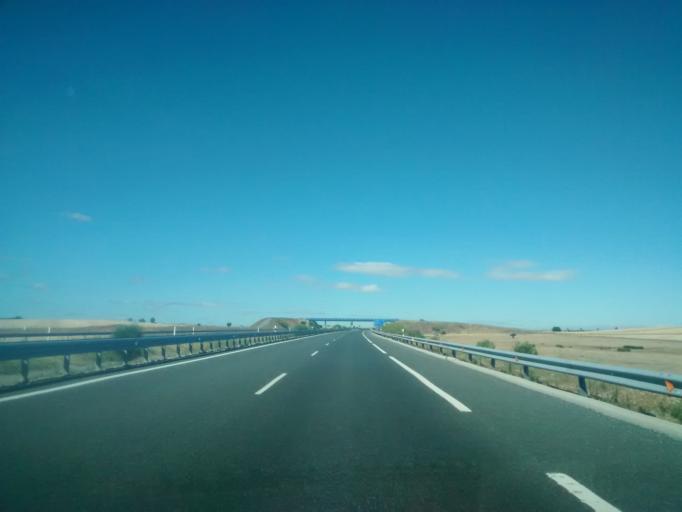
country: ES
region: Castille and Leon
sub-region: Provincia de Avila
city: Narros del Castillo
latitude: 40.8831
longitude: -5.0398
